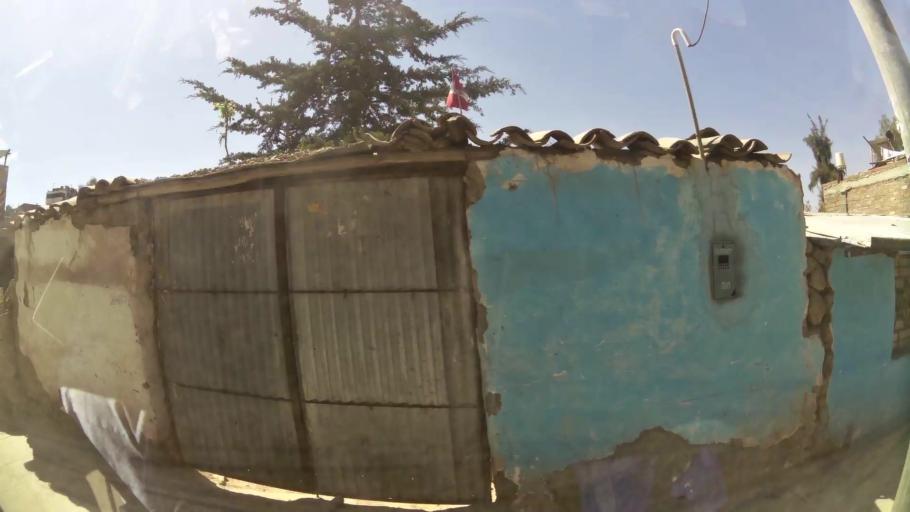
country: PE
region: Ayacucho
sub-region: Provincia de Huamanga
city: Ayacucho
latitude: -13.1651
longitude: -74.2361
